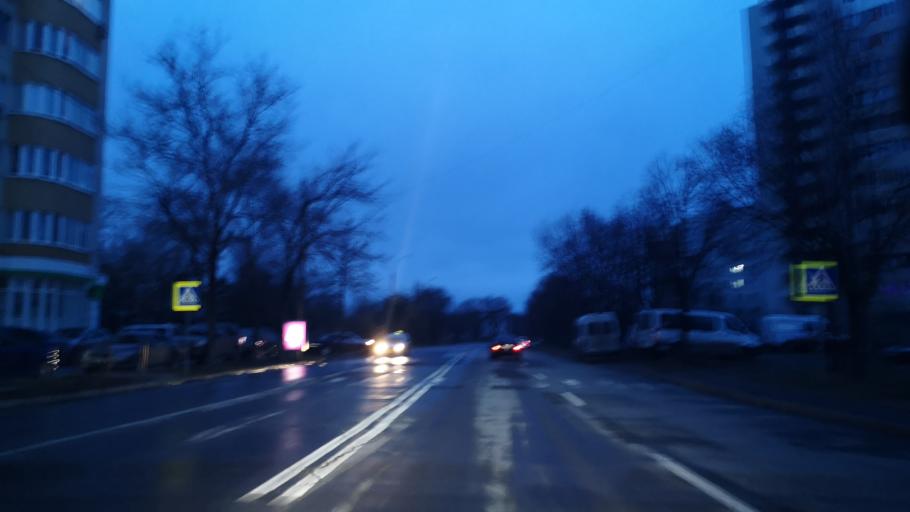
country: MD
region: Chisinau
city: Chisinau
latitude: 47.0324
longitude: 28.8786
